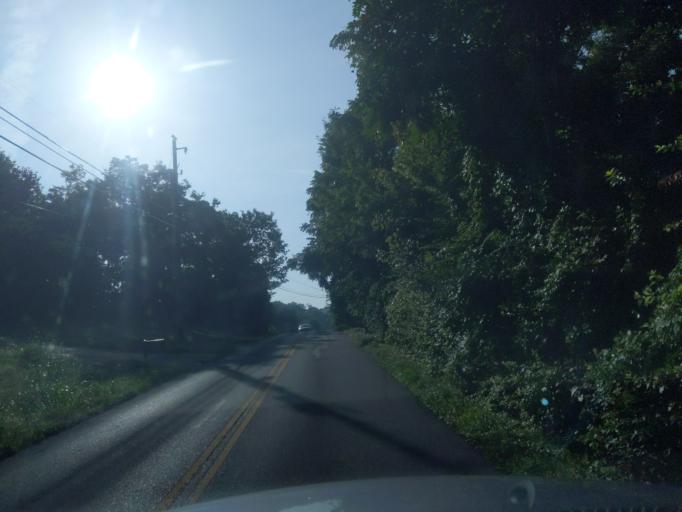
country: US
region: Tennessee
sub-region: Williamson County
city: Brentwood Estates
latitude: 36.0210
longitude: -86.7351
